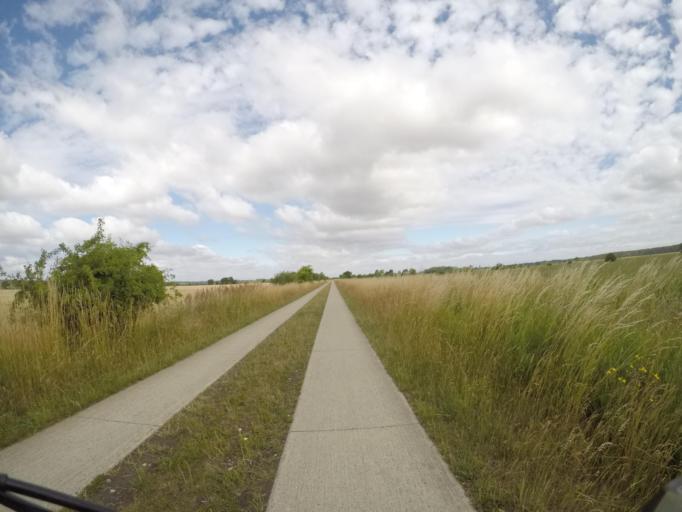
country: DE
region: Lower Saxony
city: Hitzacker
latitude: 53.1742
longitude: 11.0489
